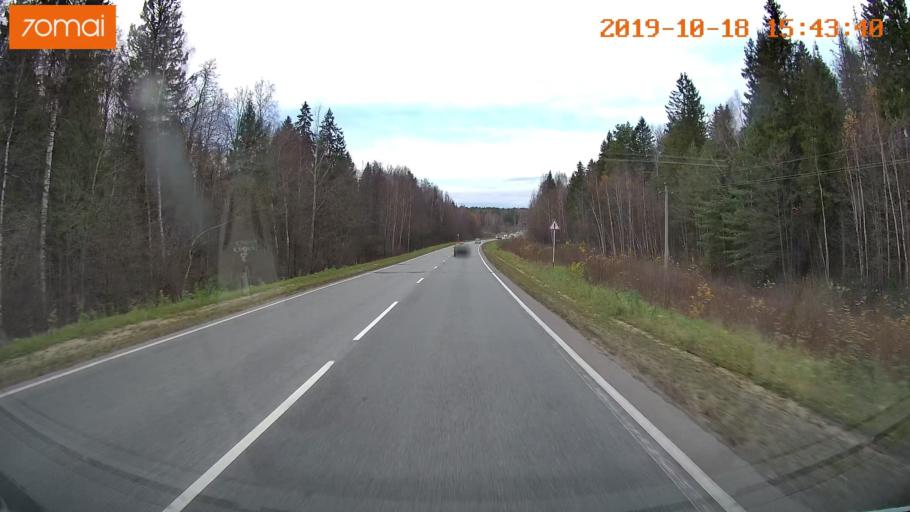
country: RU
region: Vladimir
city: Golovino
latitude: 55.9710
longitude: 40.5485
